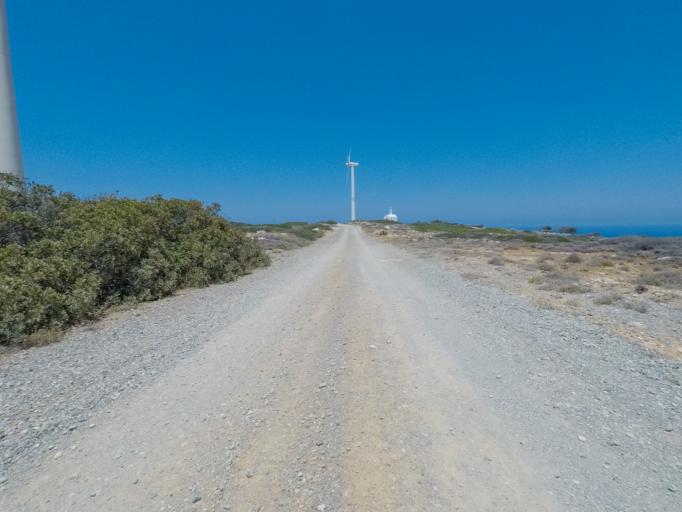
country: GR
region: Crete
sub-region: Nomos Lasithiou
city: Elounda
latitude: 35.3314
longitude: 25.7603
